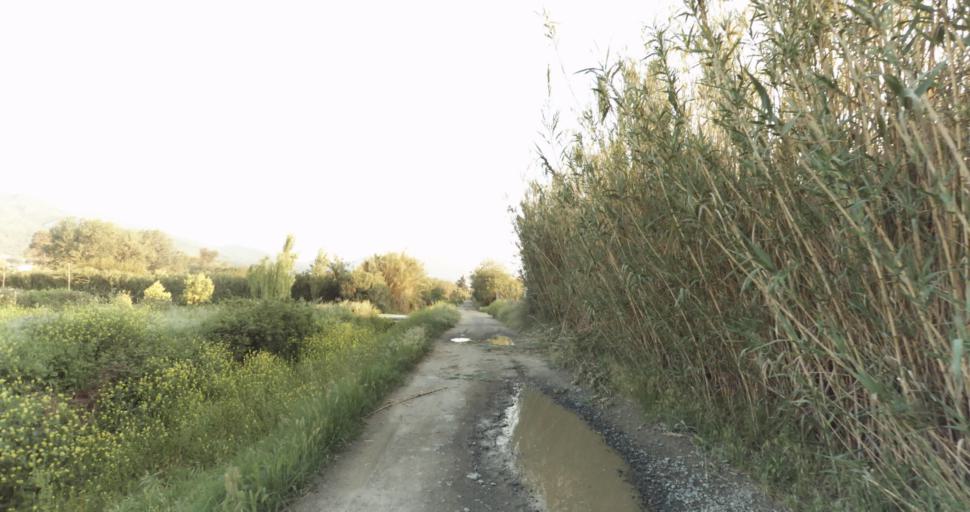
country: FR
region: Corsica
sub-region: Departement de la Haute-Corse
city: Biguglia
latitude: 42.6125
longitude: 9.4466
